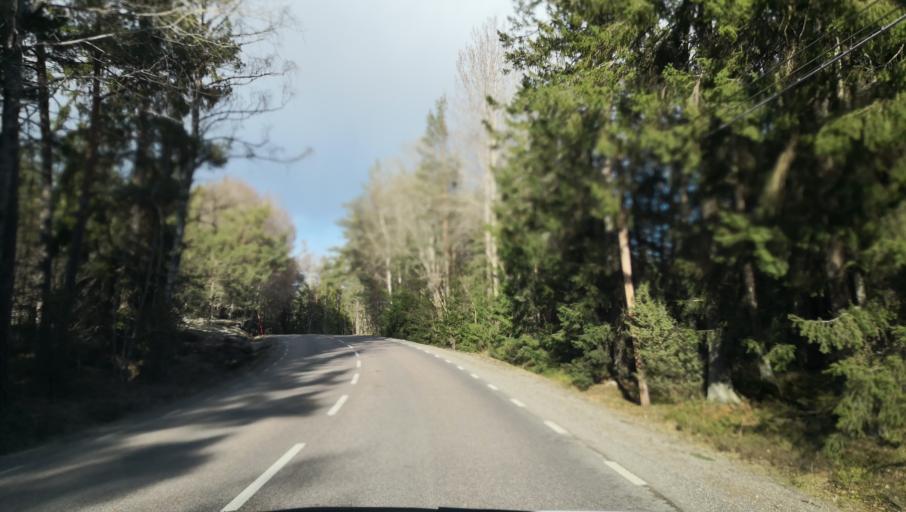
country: SE
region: Stockholm
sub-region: Varmdo Kommun
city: Hemmesta
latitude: 59.2801
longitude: 18.4803
